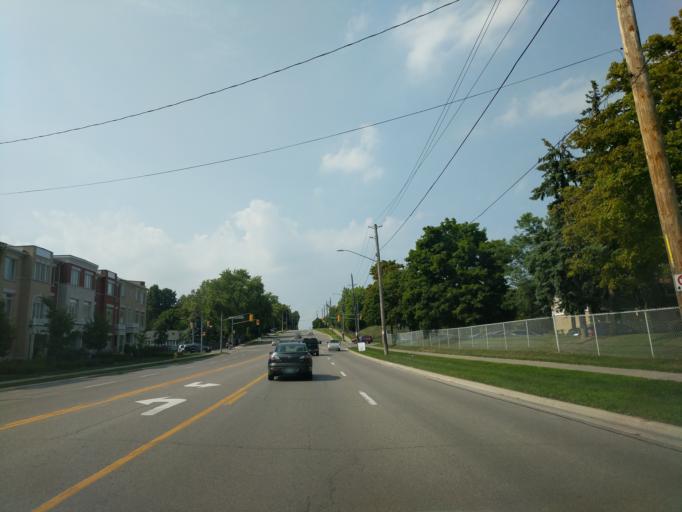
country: CA
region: Ontario
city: Ajax
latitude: 43.8380
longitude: -79.0914
